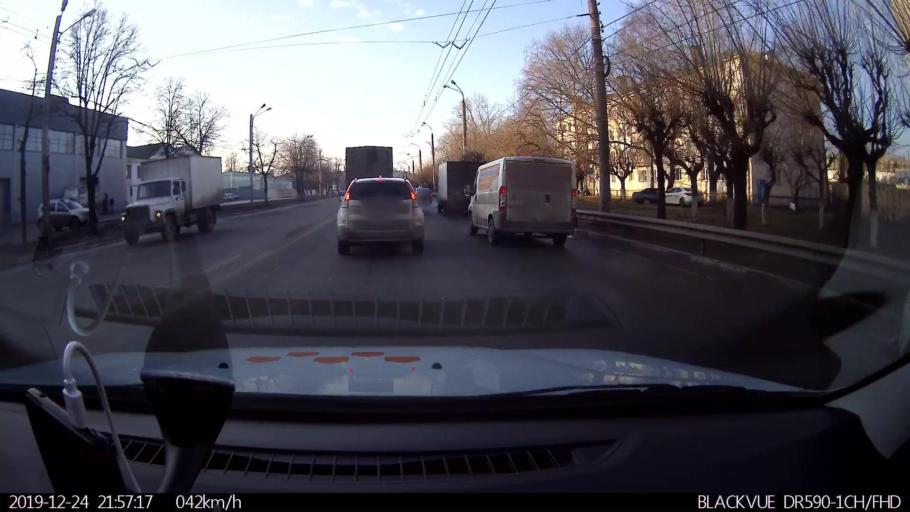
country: RU
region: Nizjnij Novgorod
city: Nizhniy Novgorod
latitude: 56.3159
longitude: 43.9083
